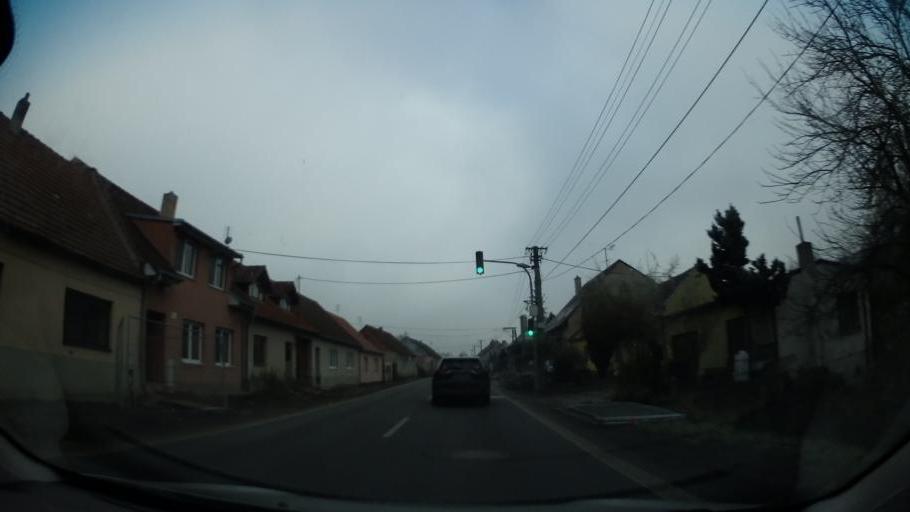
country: CZ
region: Vysocina
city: Vladislav
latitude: 49.2116
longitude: 15.9798
